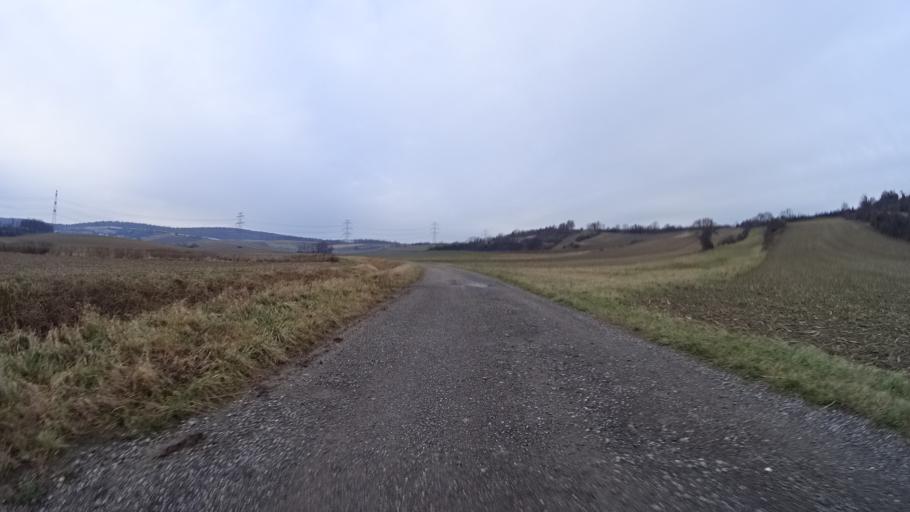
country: AT
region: Lower Austria
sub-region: Politischer Bezirk Korneuburg
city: Harmannsdorf
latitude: 48.3947
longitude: 16.3528
